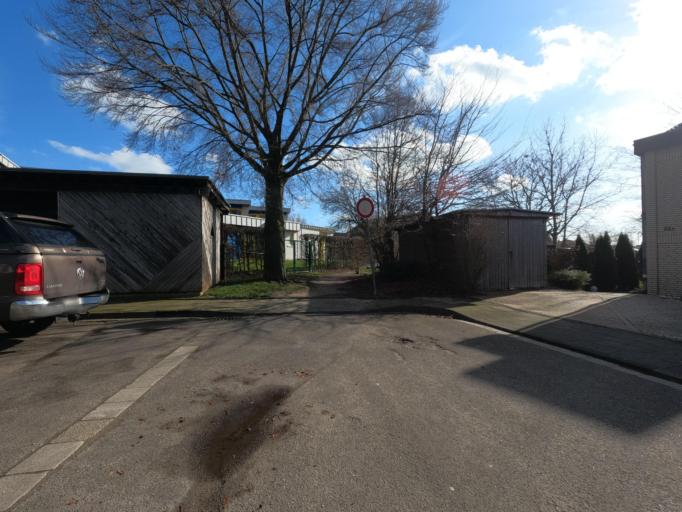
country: DE
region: North Rhine-Westphalia
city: Huckelhoven
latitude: 51.0467
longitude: 6.2196
